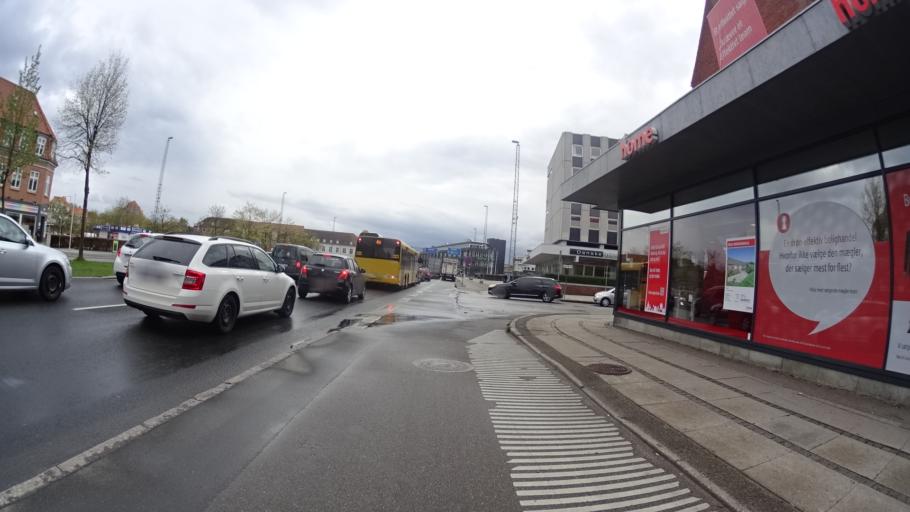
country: DK
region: Central Jutland
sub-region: Arhus Kommune
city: Stavtrup
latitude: 56.1298
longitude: 10.1641
